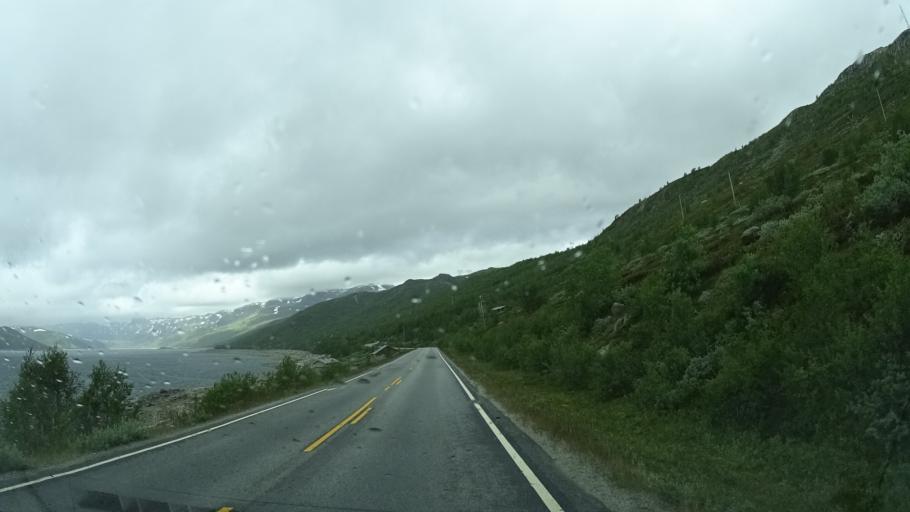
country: NO
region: Buskerud
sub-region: Hol
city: Geilo
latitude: 60.6851
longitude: 7.9190
